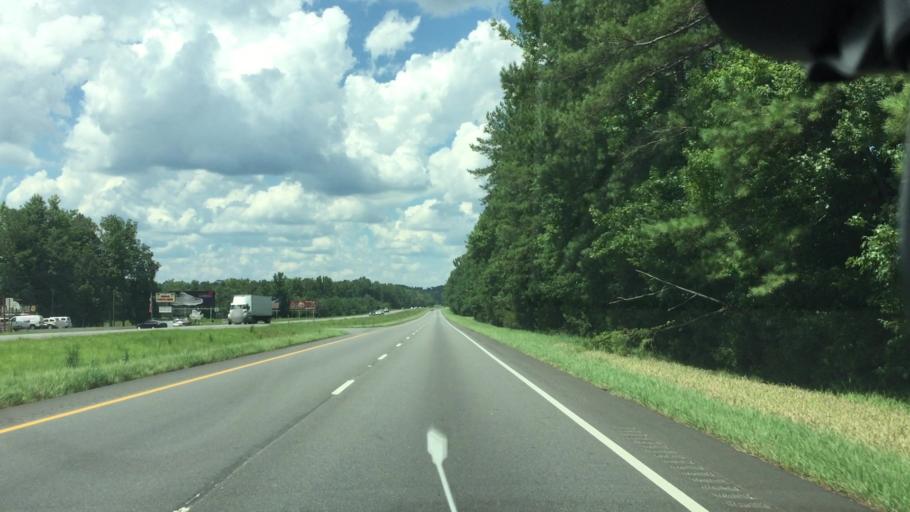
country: US
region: Alabama
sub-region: Pike County
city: Troy
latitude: 31.9195
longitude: -86.0153
